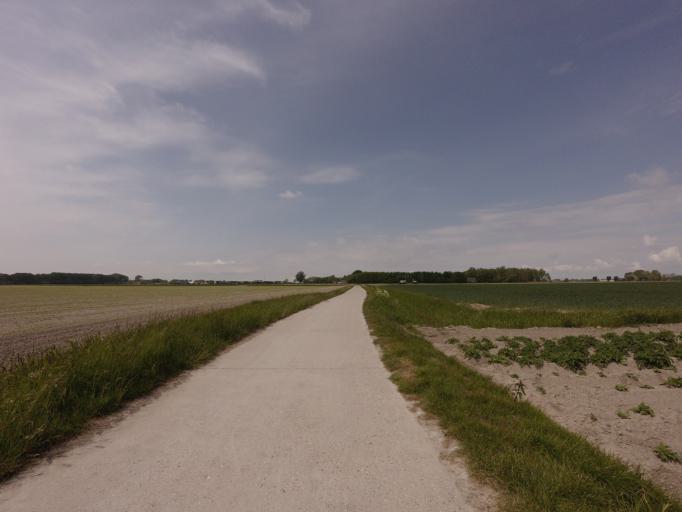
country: NL
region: Friesland
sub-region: Sudwest Fryslan
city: Bolsward
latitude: 53.1069
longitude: 5.4869
